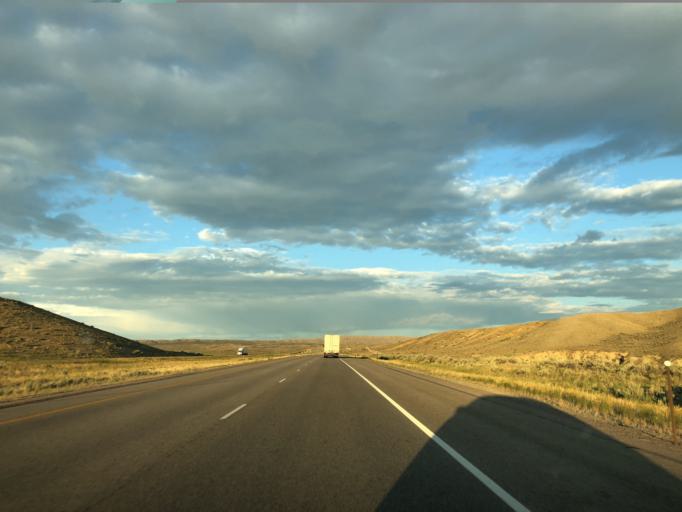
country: US
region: Wyoming
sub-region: Carbon County
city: Saratoga
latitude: 41.7348
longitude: -106.7365
